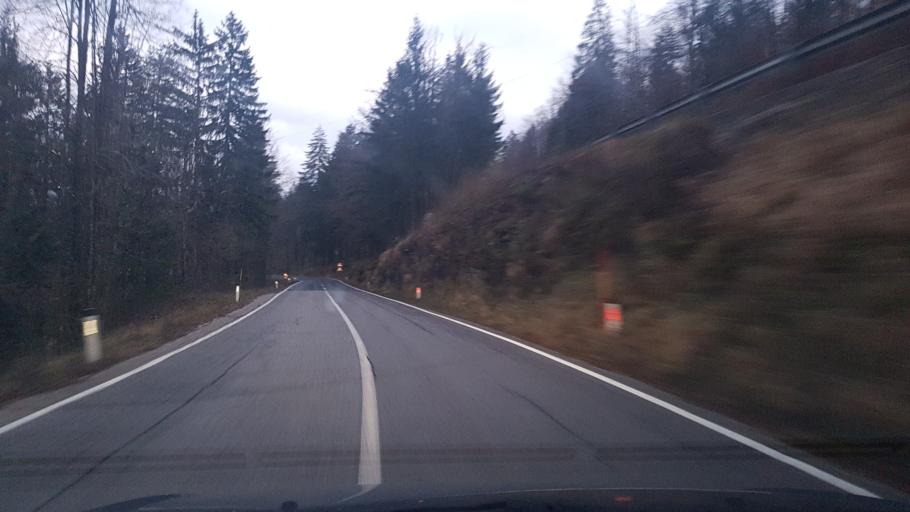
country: SI
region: Idrija
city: Idrija
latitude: 45.9544
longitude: 14.0759
